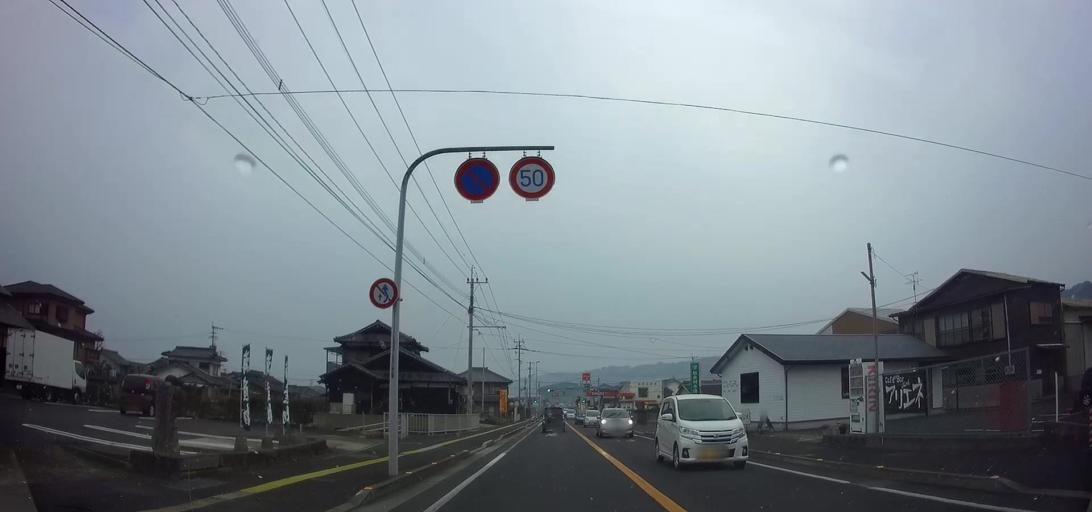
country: JP
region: Nagasaki
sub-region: Isahaya-shi
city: Isahaya
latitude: 32.7875
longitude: 130.1936
